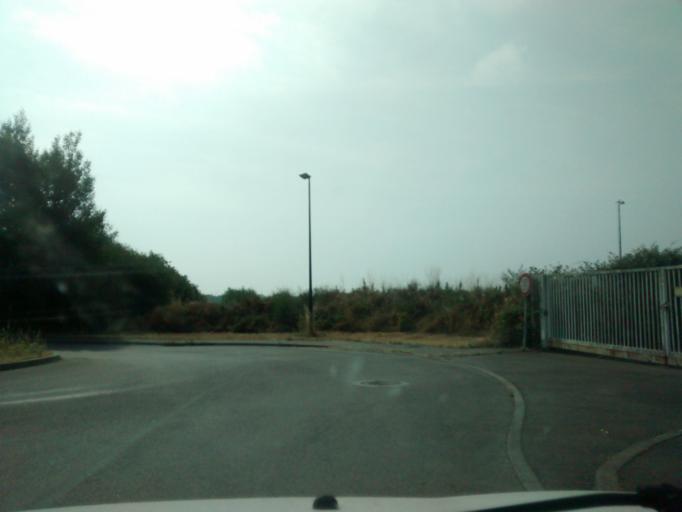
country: FR
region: Brittany
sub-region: Departement d'Ille-et-Vilaine
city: Saint-Jacques-de-la-Lande
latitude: 48.0739
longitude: -1.7222
